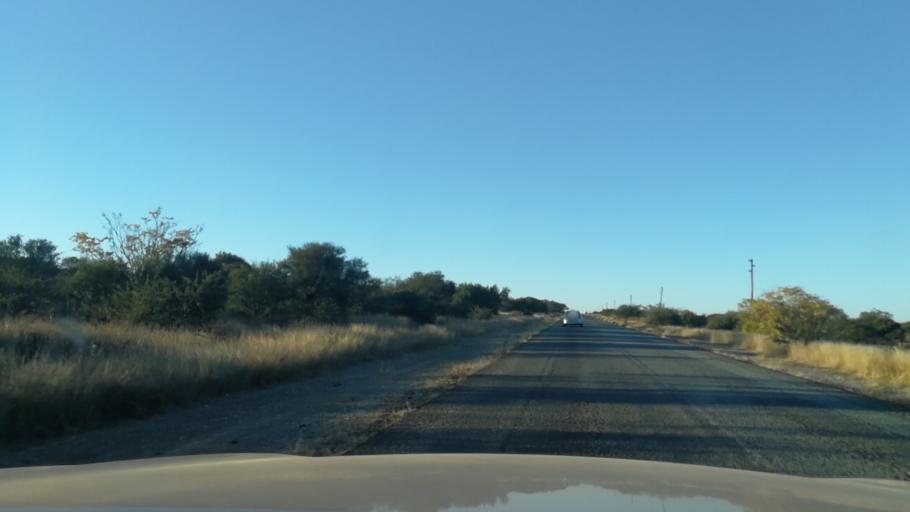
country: ZA
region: North-West
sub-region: Bojanala Platinum District Municipality
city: Koster
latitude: -25.7400
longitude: 26.7496
